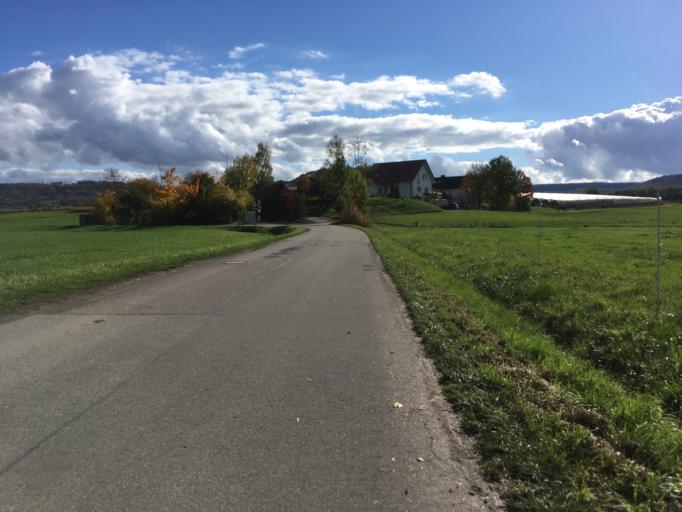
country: DE
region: Baden-Wuerttemberg
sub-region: Regierungsbezirk Stuttgart
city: Pfedelbach
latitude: 49.1754
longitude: 9.5326
